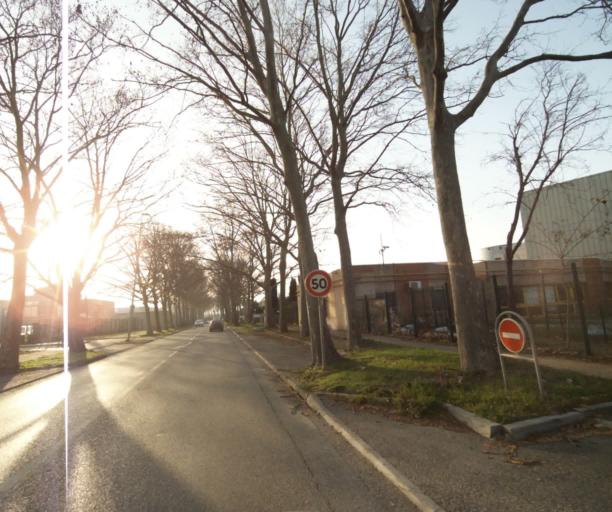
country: FR
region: Provence-Alpes-Cote d'Azur
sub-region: Departement des Bouches-du-Rhone
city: Saint-Victoret
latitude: 43.4231
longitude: 5.2572
